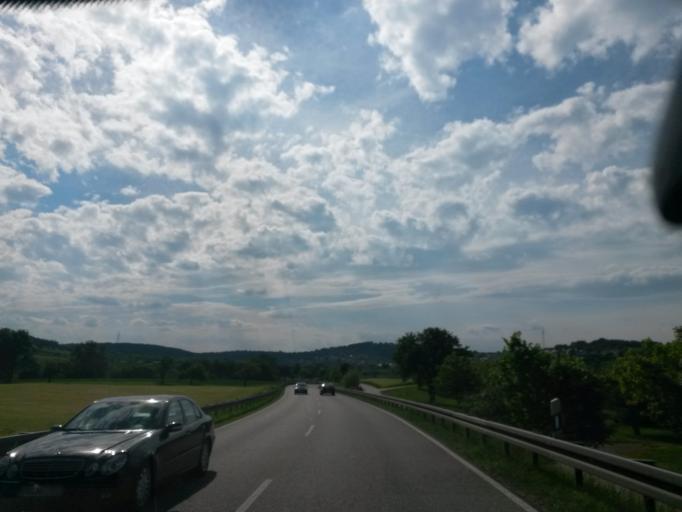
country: DE
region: Baden-Wuerttemberg
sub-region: Karlsruhe Region
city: Simmozheim
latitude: 48.7488
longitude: 8.8321
